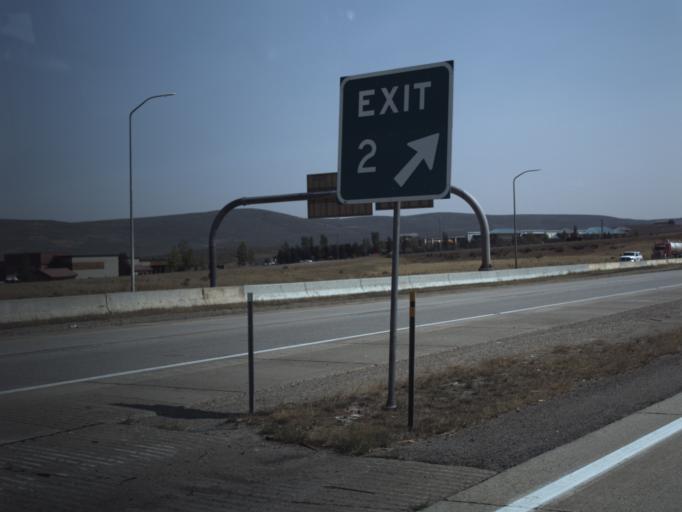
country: US
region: Utah
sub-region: Summit County
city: Snyderville
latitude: 40.7204
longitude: -111.4894
